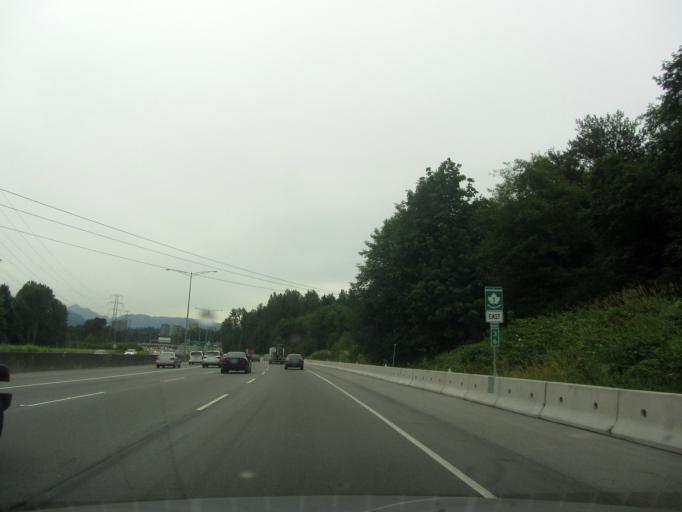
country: CA
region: British Columbia
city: Burnaby
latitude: 49.2460
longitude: -122.9702
